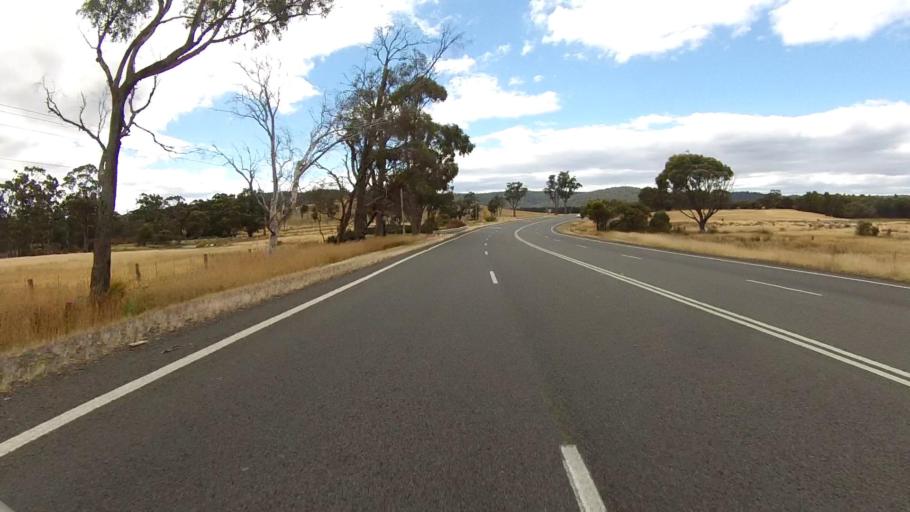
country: AU
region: Tasmania
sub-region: Sorell
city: Sorell
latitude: -42.6411
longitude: 147.5793
